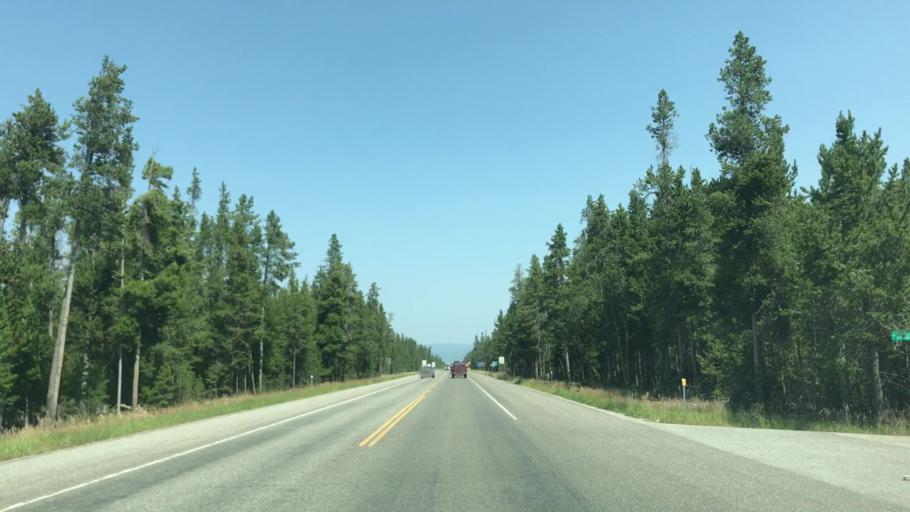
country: US
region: Montana
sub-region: Gallatin County
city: West Yellowstone
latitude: 44.6678
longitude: -111.1000
